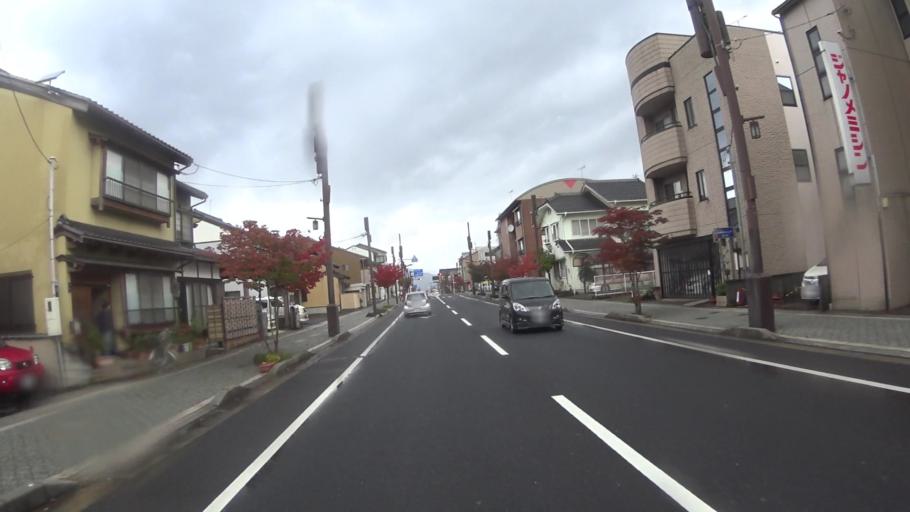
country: JP
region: Kyoto
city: Miyazu
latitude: 35.5341
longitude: 135.1934
